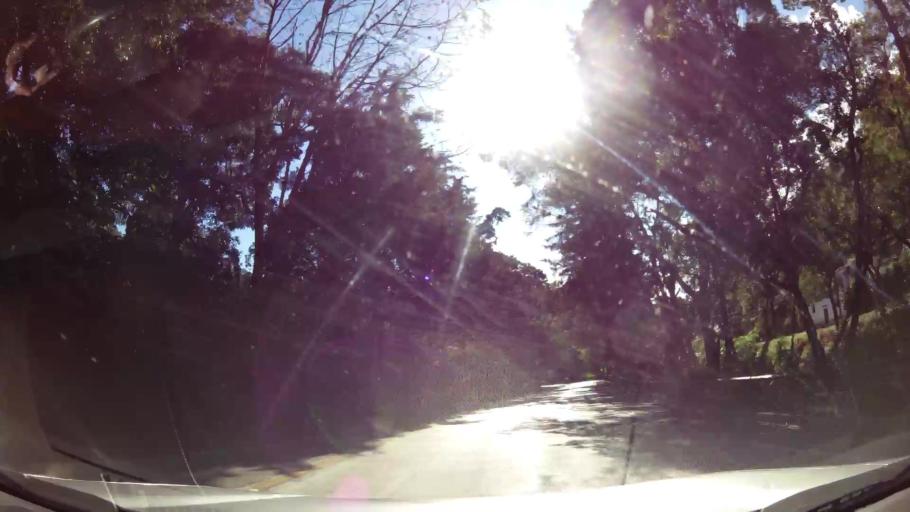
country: GT
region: Sacatepequez
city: Santa Lucia Milpas Altas
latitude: 14.5619
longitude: -90.7026
